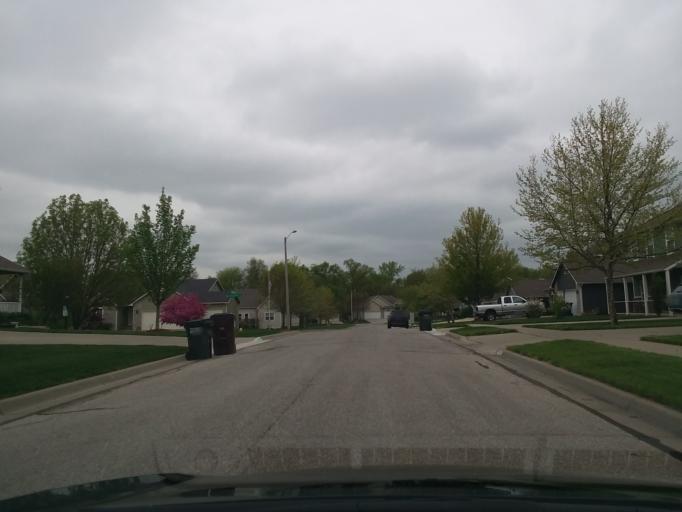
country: US
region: Kansas
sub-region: Douglas County
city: Lawrence
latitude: 38.9909
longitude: -95.2769
